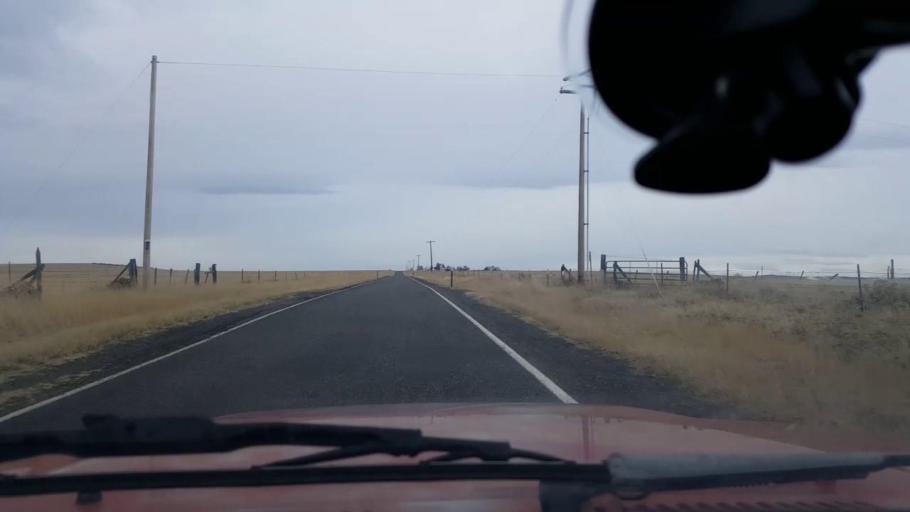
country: US
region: Washington
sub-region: Asotin County
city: Clarkston Heights-Vineland
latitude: 46.3241
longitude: -117.3261
